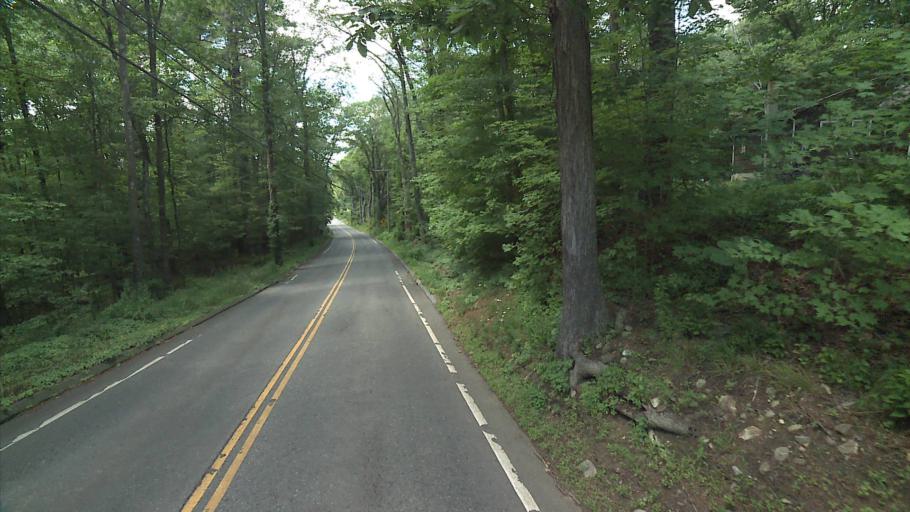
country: US
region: Massachusetts
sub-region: Worcester County
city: Southbridge
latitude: 41.9782
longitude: -72.0743
